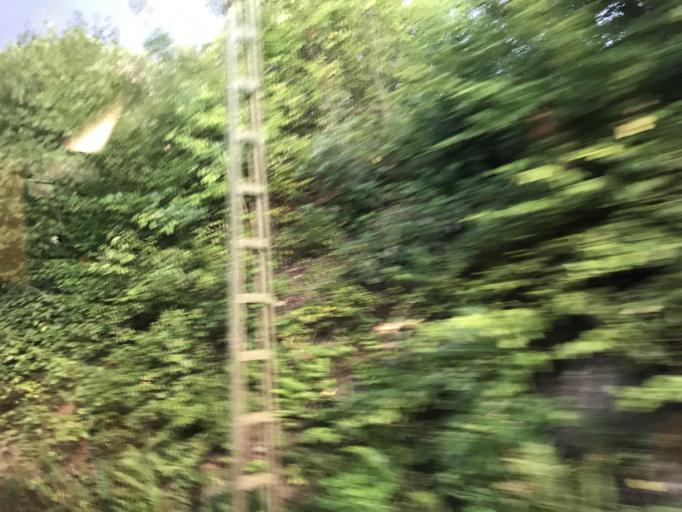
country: DE
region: Rheinland-Pfalz
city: Kirchen
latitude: 50.8160
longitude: 7.8990
